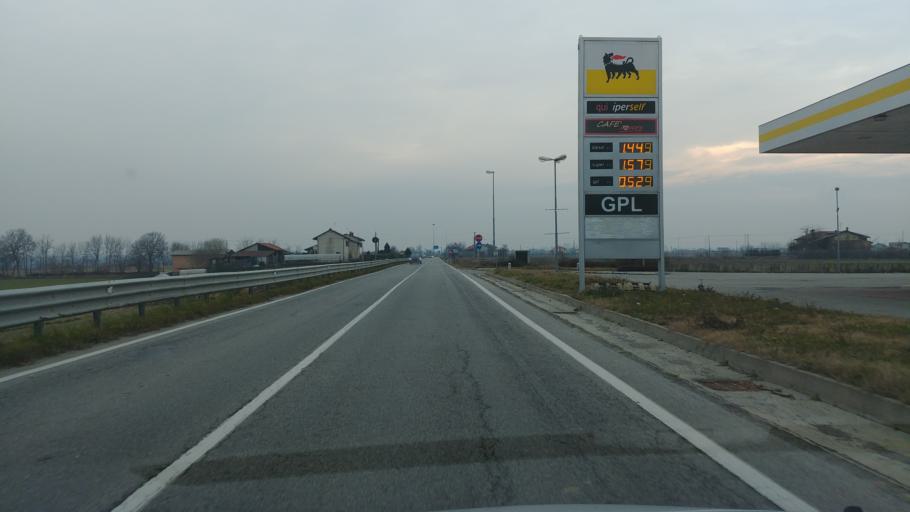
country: IT
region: Piedmont
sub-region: Provincia di Cuneo
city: Castelletto Stura
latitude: 44.4640
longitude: 7.6321
